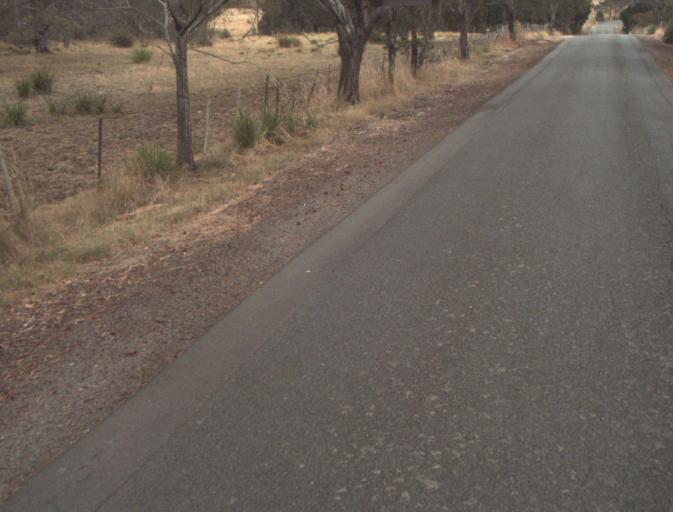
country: AU
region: Tasmania
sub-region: Launceston
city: Mayfield
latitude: -41.2826
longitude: 147.0275
